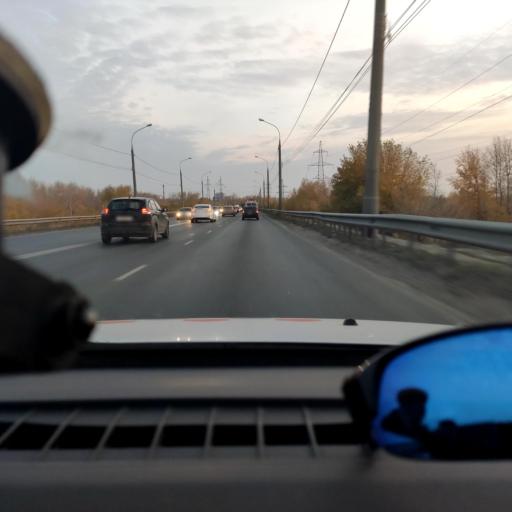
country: RU
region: Samara
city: Samara
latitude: 53.1608
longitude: 50.1934
